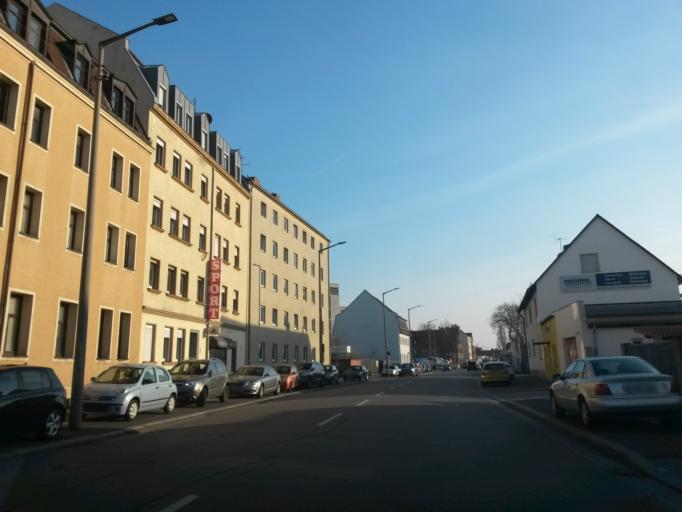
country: DE
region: Bavaria
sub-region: Regierungsbezirk Mittelfranken
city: Furth
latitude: 49.4603
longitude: 11.0108
